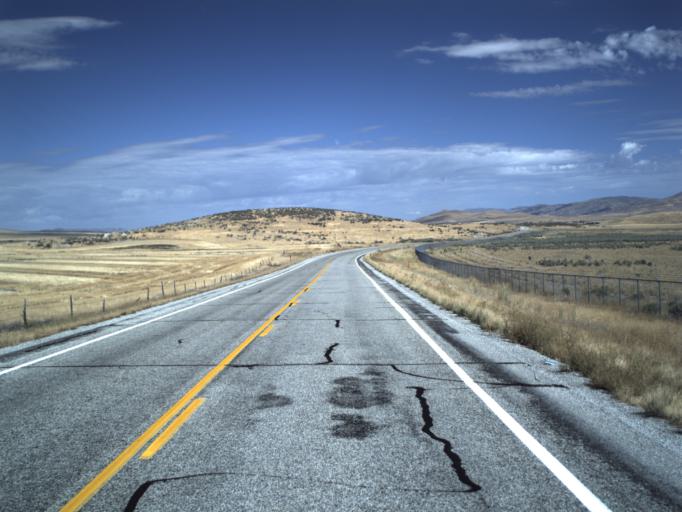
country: US
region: Utah
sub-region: Box Elder County
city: Tremonton
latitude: 41.7124
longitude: -112.4526
